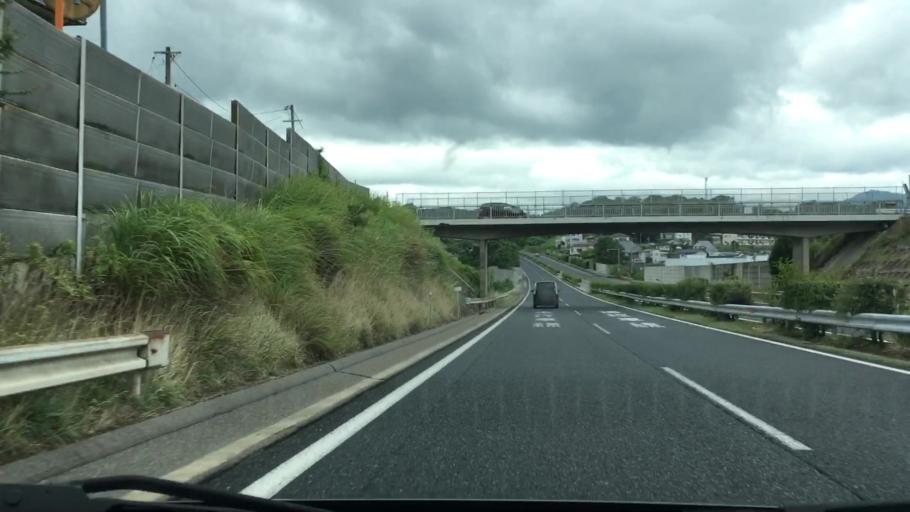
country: JP
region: Okayama
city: Tsuyama
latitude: 35.0746
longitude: 134.0206
